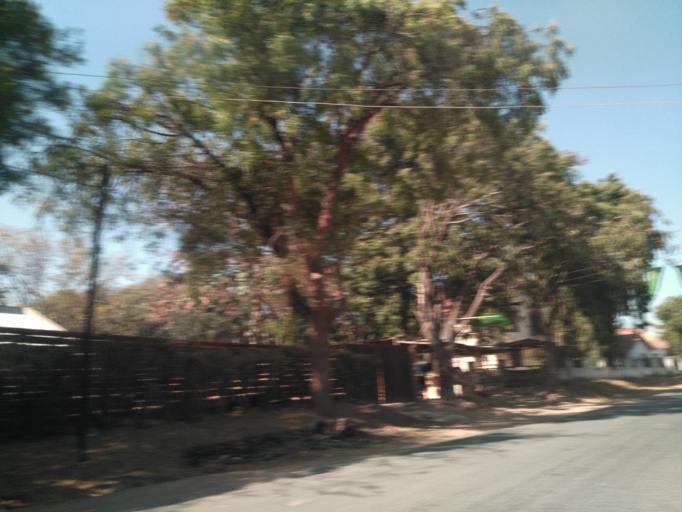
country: TZ
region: Dodoma
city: Dodoma
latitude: -6.1676
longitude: 35.7521
